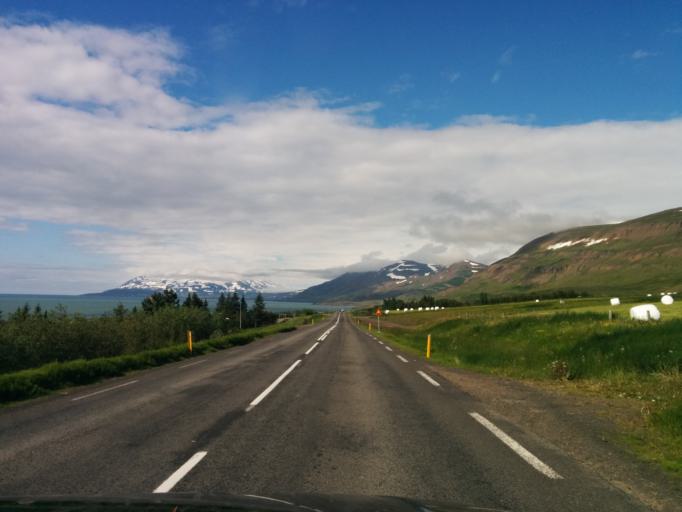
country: IS
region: Northeast
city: Akureyri
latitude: 65.7704
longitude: -18.0706
